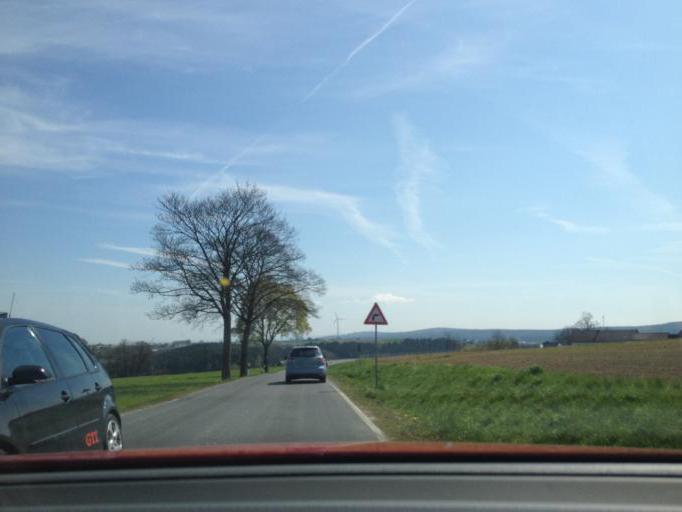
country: DE
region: Bavaria
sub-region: Upper Franconia
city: Thiersheim
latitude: 50.0695
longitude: 12.1471
